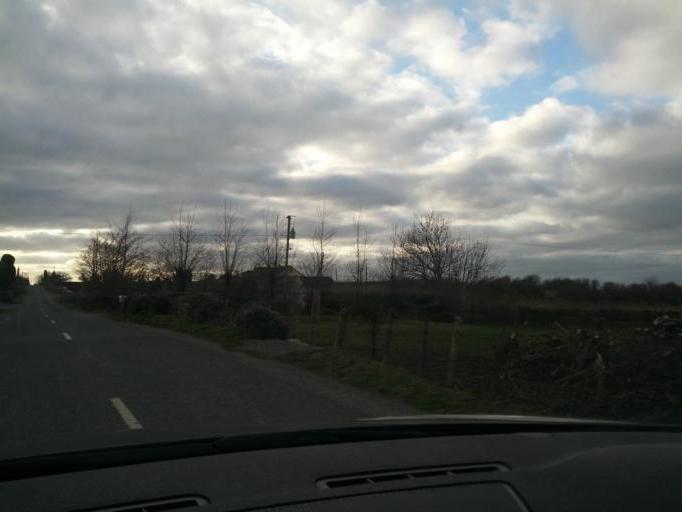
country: IE
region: Leinster
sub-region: Uibh Fhaili
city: Ferbane
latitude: 53.3236
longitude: -7.9021
